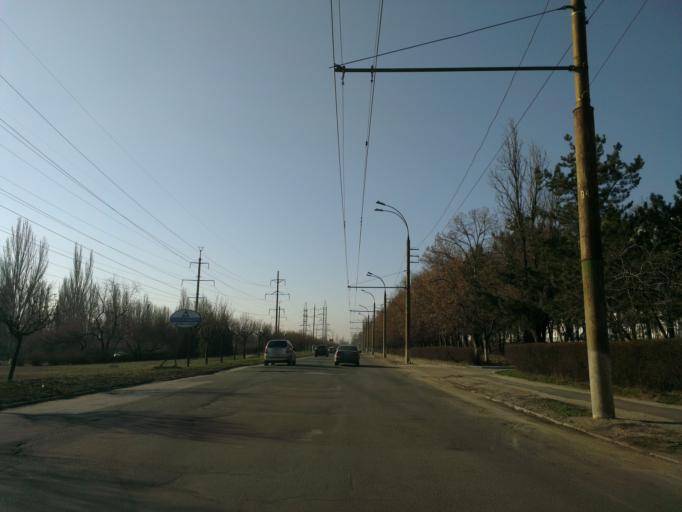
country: MD
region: Chisinau
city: Chisinau
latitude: 47.0243
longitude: 28.8879
